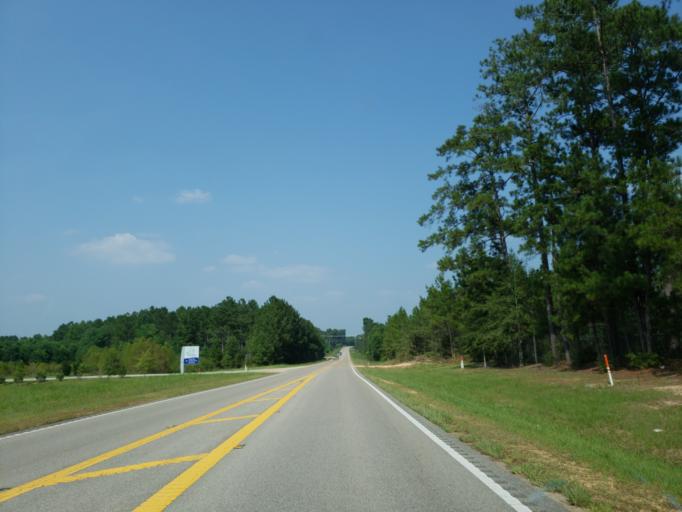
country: US
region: Mississippi
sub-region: Jones County
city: Ellisville
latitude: 31.5745
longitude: -89.2322
